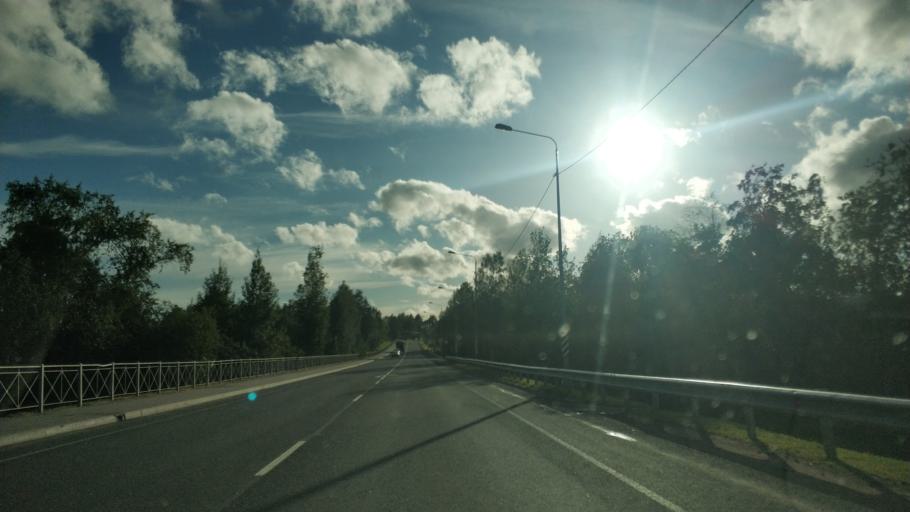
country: RU
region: Leningrad
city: Sapernoye
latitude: 60.7151
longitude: 30.0487
